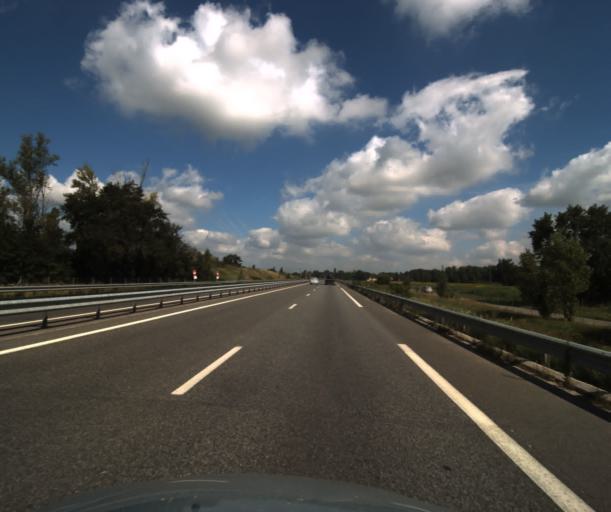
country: FR
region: Midi-Pyrenees
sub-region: Departement de la Haute-Garonne
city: Labarthe-sur-Leze
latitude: 43.4744
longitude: 1.4084
